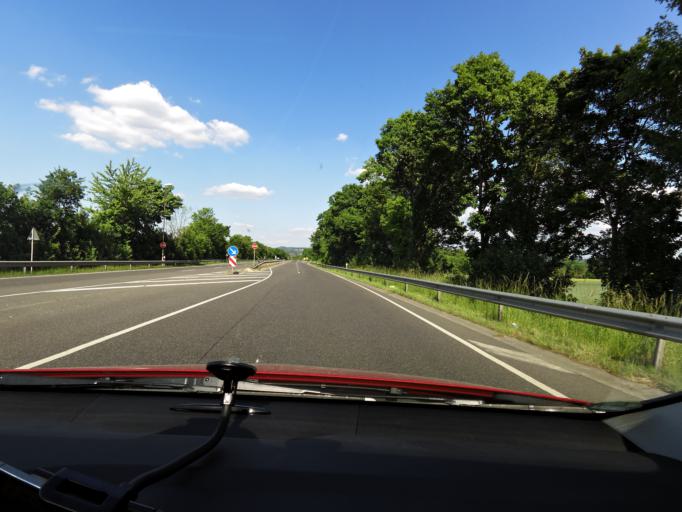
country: DE
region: Rheinland-Pfalz
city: Sinzig
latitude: 50.5540
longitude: 7.2373
